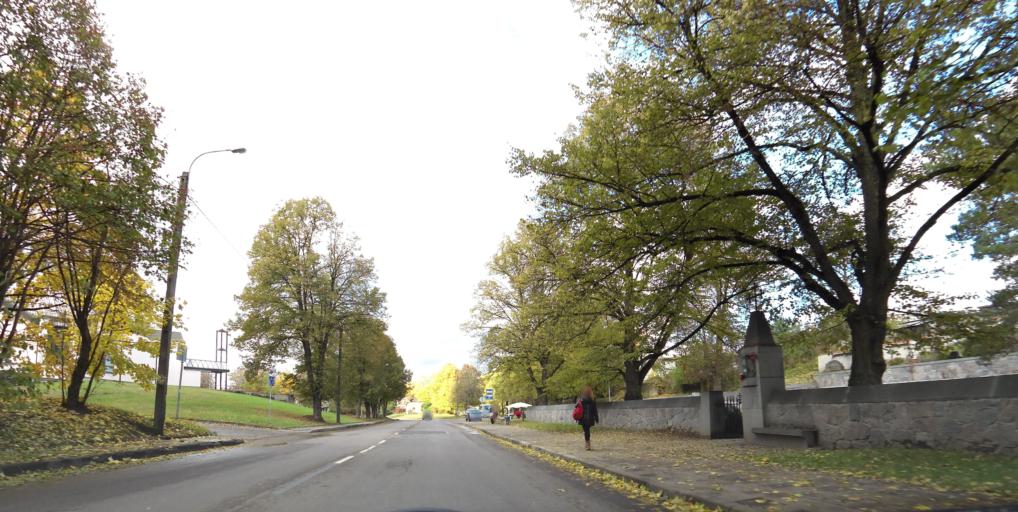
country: LT
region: Vilnius County
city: Rasos
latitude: 54.6701
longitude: 25.3012
